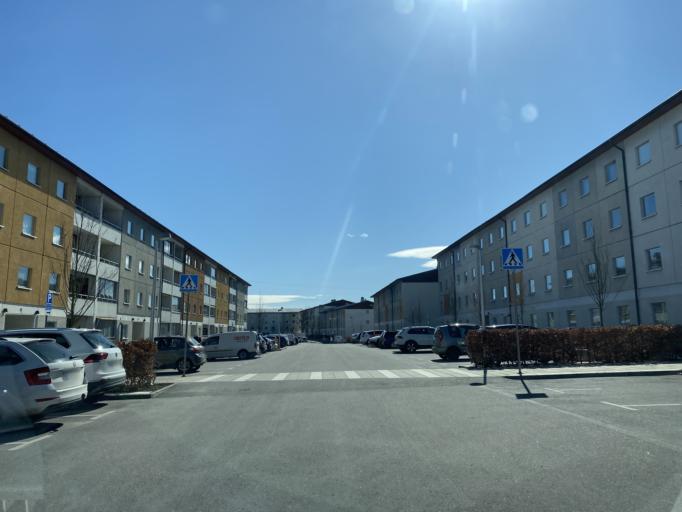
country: SE
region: Stockholm
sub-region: Stockholms Kommun
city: Arsta
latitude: 59.2843
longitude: 18.0381
